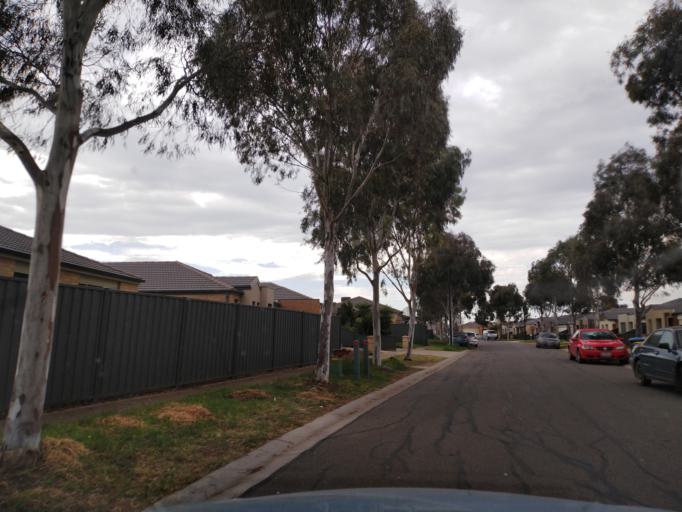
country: AU
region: Victoria
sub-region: Wyndham
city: Williams Landing
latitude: -37.8398
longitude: 144.7155
